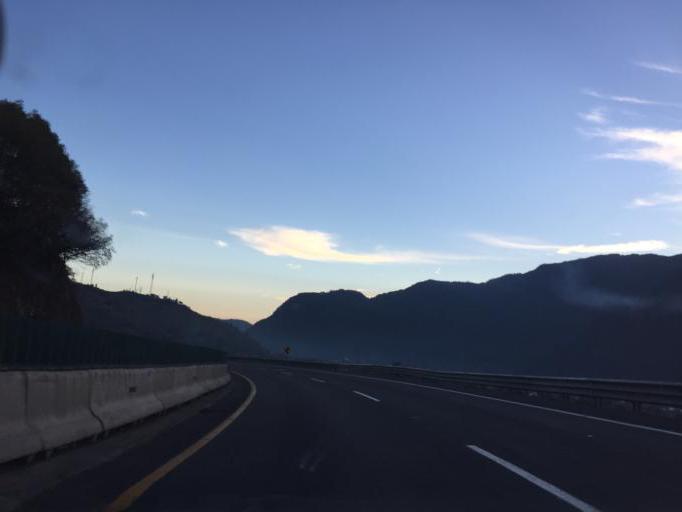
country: MX
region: Veracruz
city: Ciudad Mendoza
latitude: 18.8125
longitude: -97.1796
